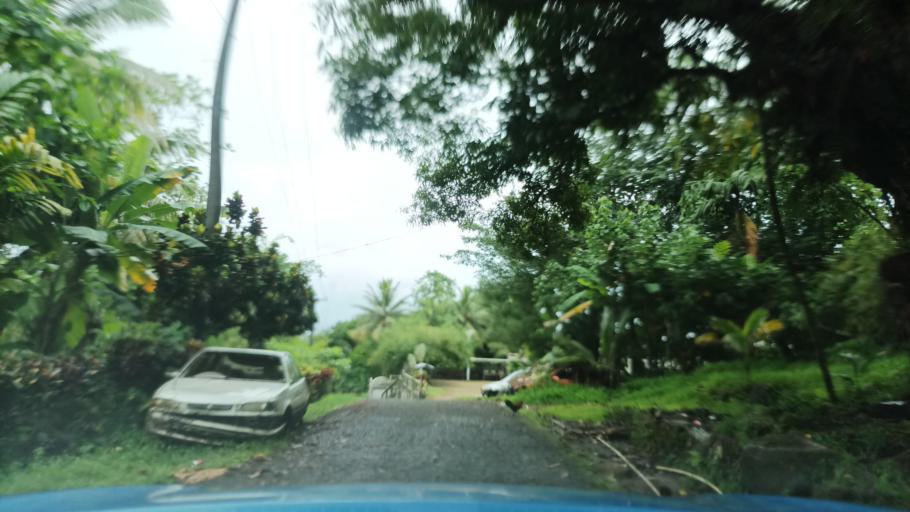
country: FM
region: Pohnpei
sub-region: Sokehs Municipality
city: Palikir - National Government Center
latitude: 6.8338
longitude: 158.1705
